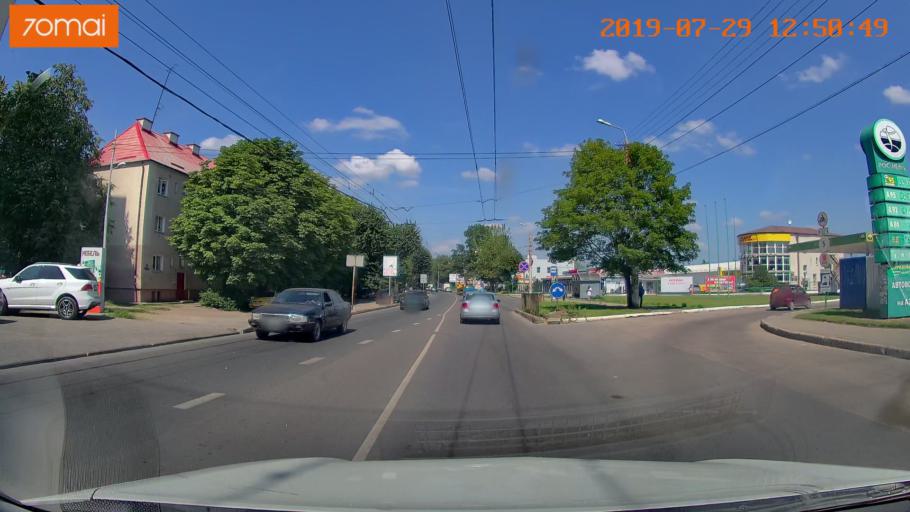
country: RU
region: Kaliningrad
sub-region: Gorod Kaliningrad
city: Kaliningrad
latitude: 54.6894
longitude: 20.5318
